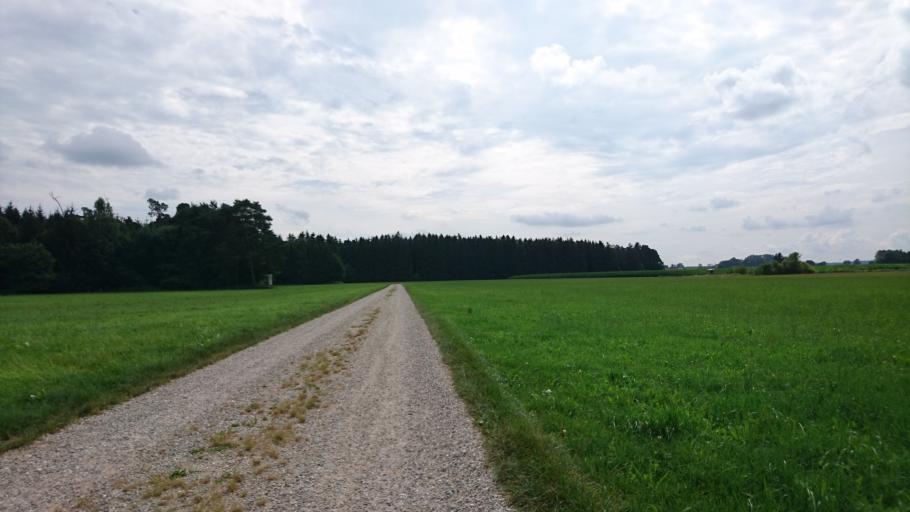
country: DE
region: Bavaria
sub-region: Swabia
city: Dinkelscherben
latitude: 48.3461
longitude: 10.6130
